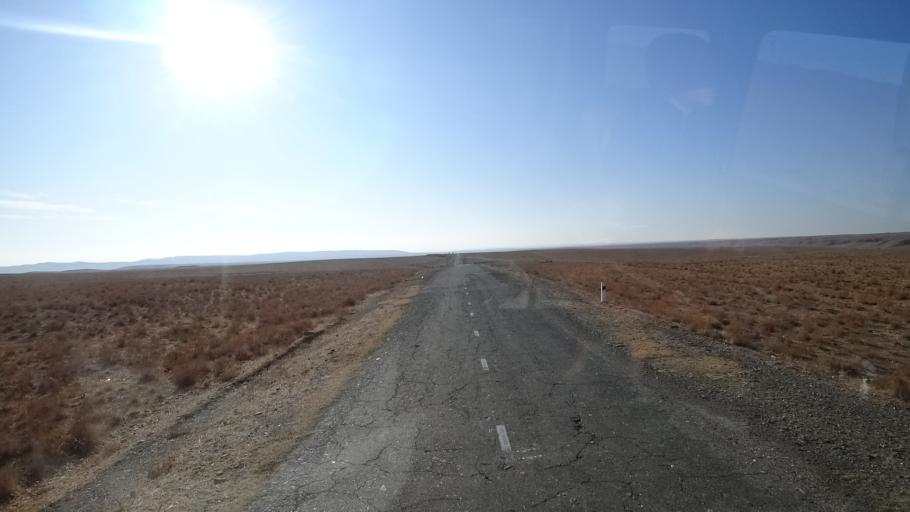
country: UZ
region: Navoiy
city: Karmana Shahri
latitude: 40.2783
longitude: 65.5553
